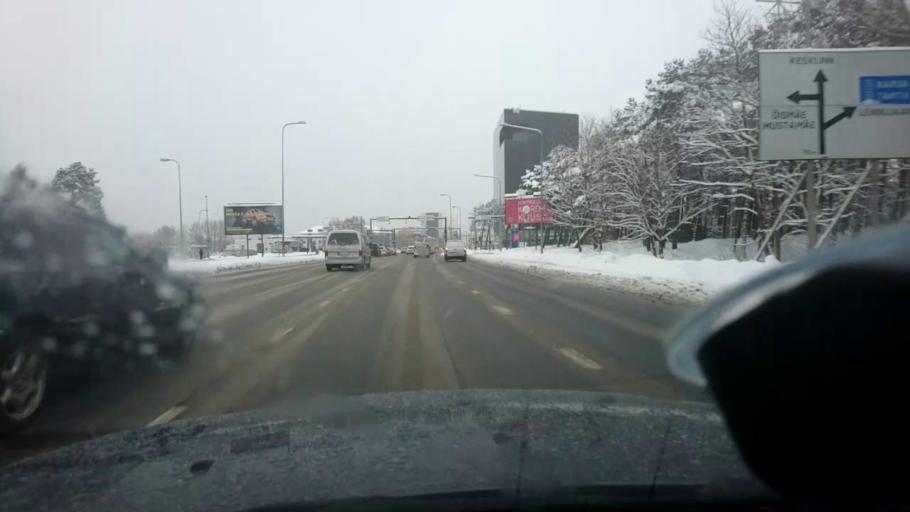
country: EE
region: Harju
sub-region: Tallinna linn
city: Tallinn
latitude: 59.4008
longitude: 24.7283
